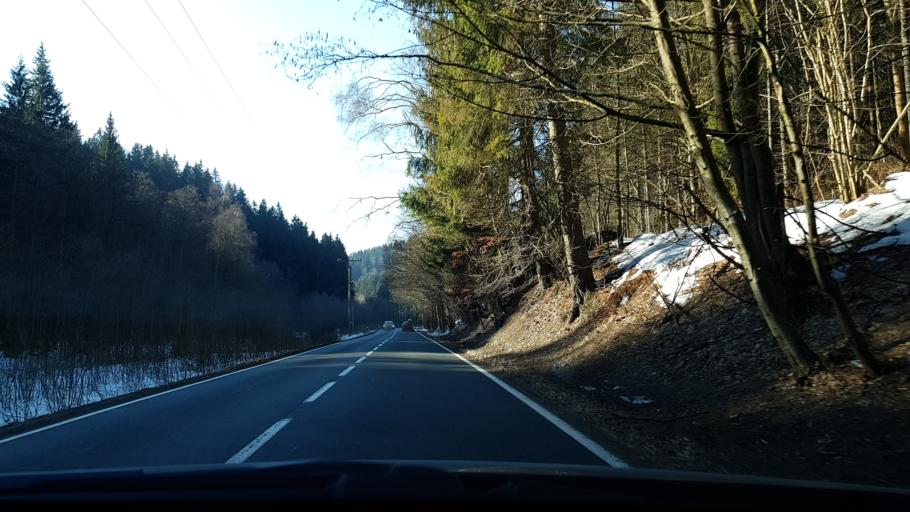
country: CZ
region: Olomoucky
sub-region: Okres Sumperk
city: Stare Mesto
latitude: 50.1276
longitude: 17.0108
